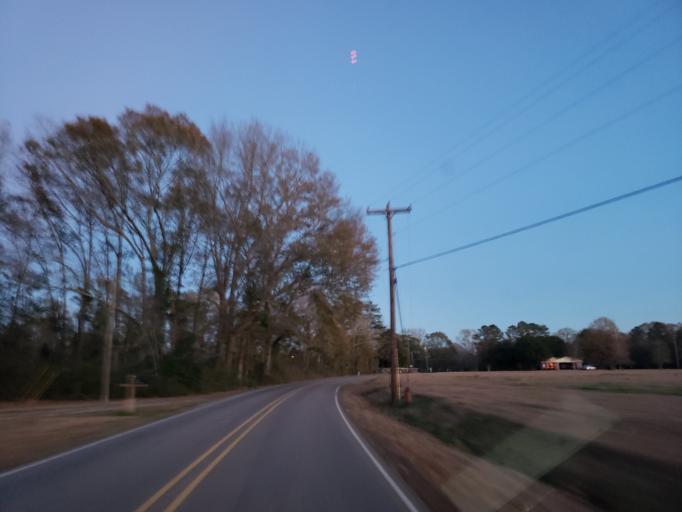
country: US
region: Mississippi
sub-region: Forrest County
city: Rawls Springs
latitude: 31.4250
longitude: -89.3392
